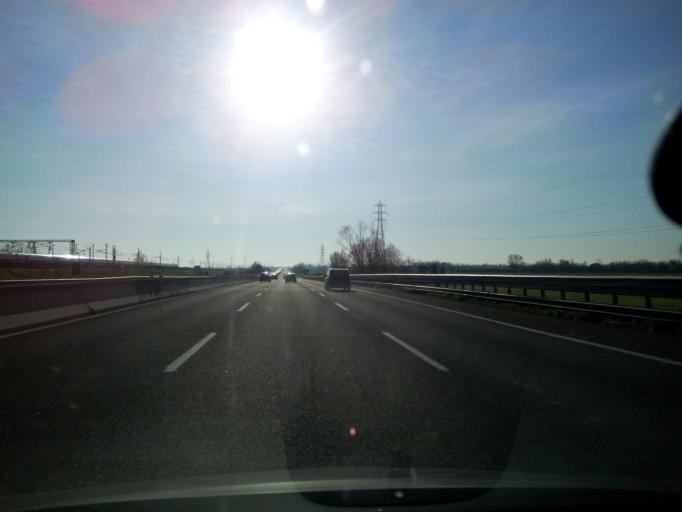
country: IT
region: Emilia-Romagna
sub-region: Provincia di Reggio Emilia
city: Reggio nell'Emilia
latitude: 44.7233
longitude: 10.6563
